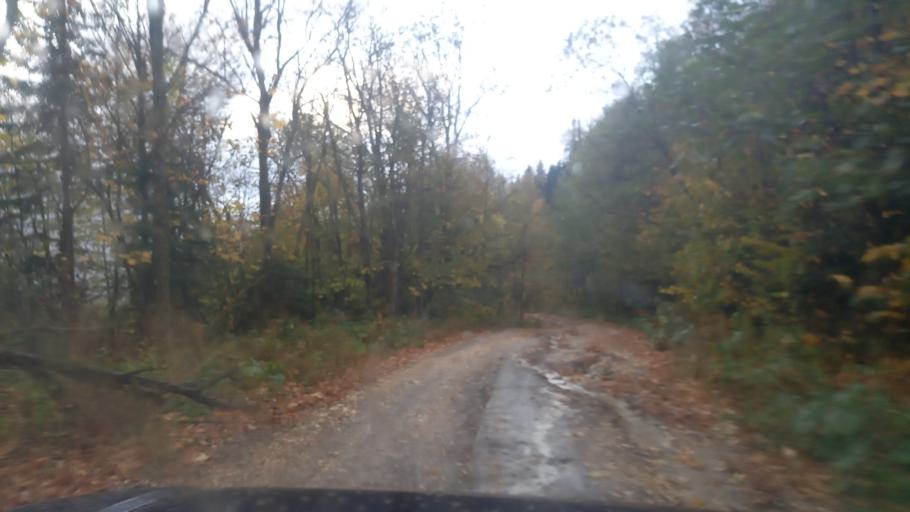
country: RU
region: Krasnodarskiy
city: Neftegorsk
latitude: 44.0208
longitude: 39.8412
